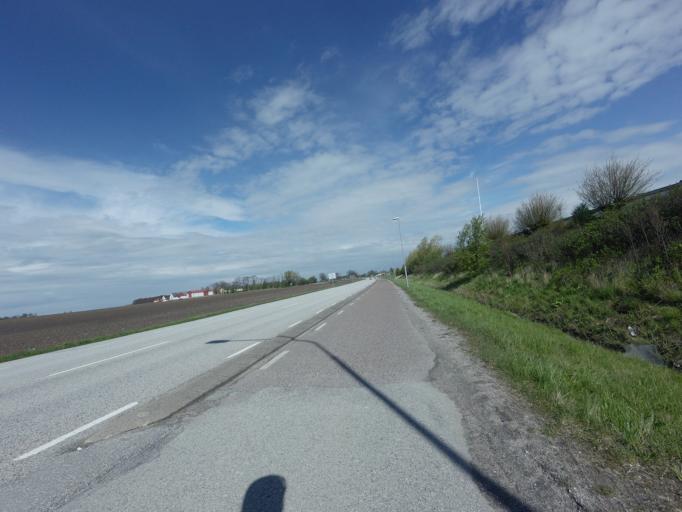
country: SE
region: Skane
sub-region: Vellinge Kommun
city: Vellinge
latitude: 55.4824
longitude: 13.0143
